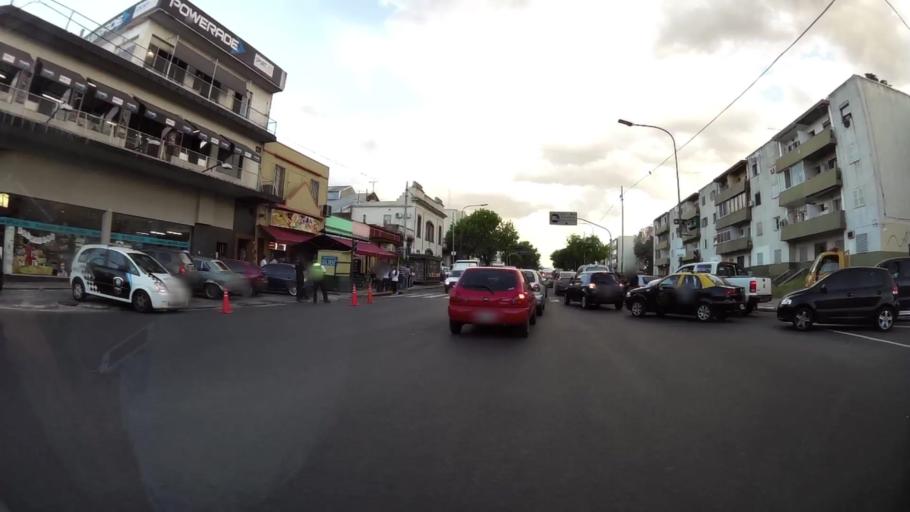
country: AR
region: Buenos Aires
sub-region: Partido de General San Martin
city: General San Martin
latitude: -34.5700
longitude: -58.5092
